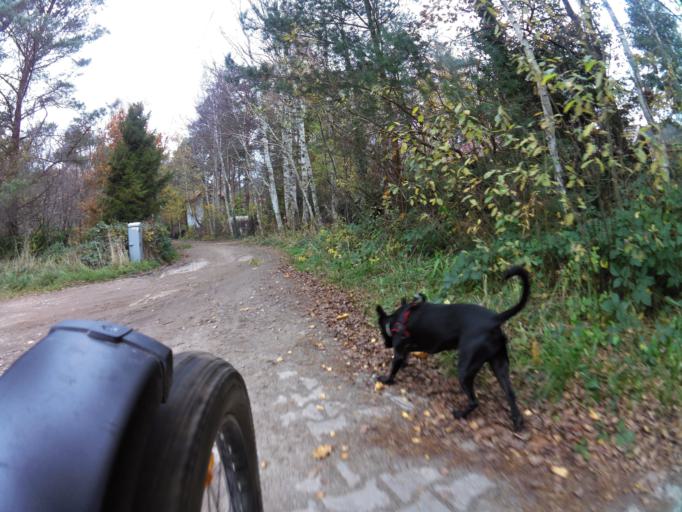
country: PL
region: Pomeranian Voivodeship
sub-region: Powiat pucki
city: Wierzchucino
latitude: 54.8277
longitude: 18.0815
